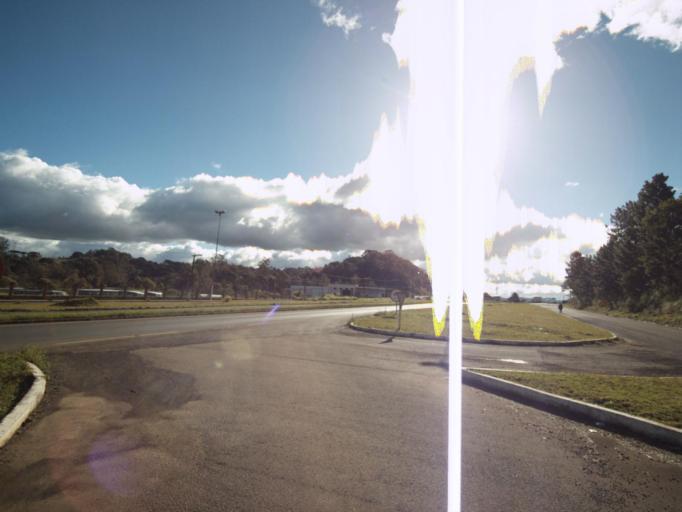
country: BR
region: Santa Catarina
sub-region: Joacaba
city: Joacaba
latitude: -27.1814
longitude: -51.5212
